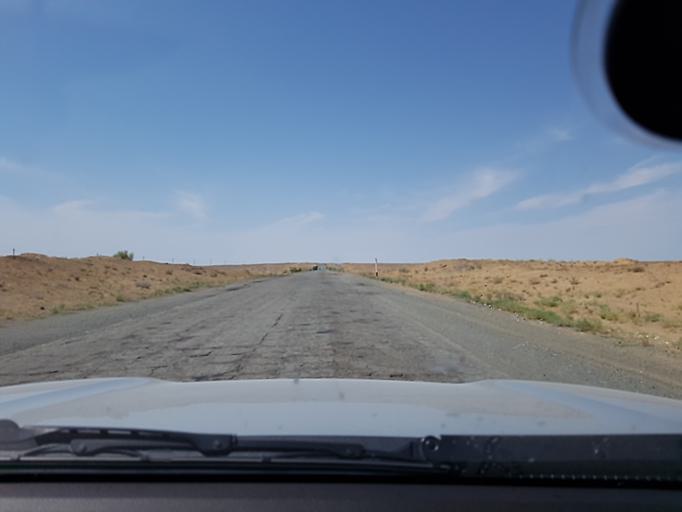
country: UZ
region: Karakalpakstan
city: Mang'it Shahri
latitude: 42.2887
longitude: 60.0755
